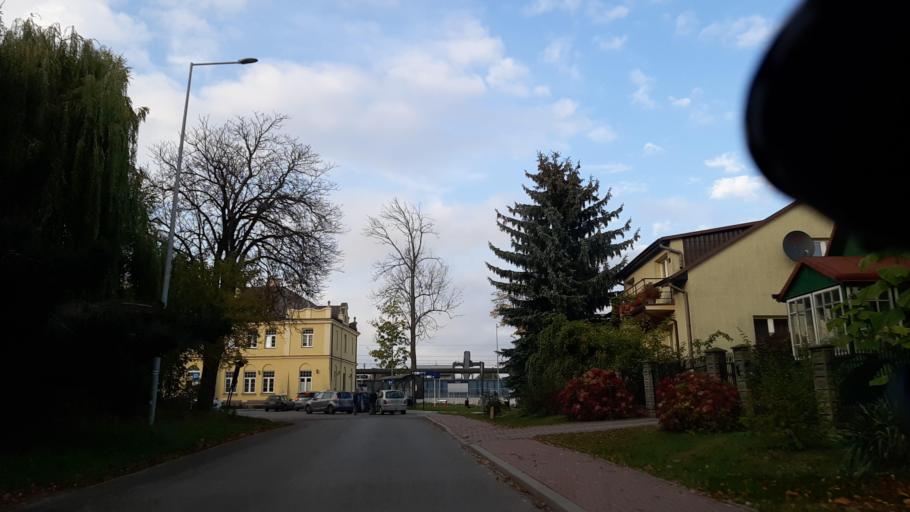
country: PL
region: Lublin Voivodeship
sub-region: Powiat pulawski
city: Naleczow
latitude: 51.3170
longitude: 22.2133
